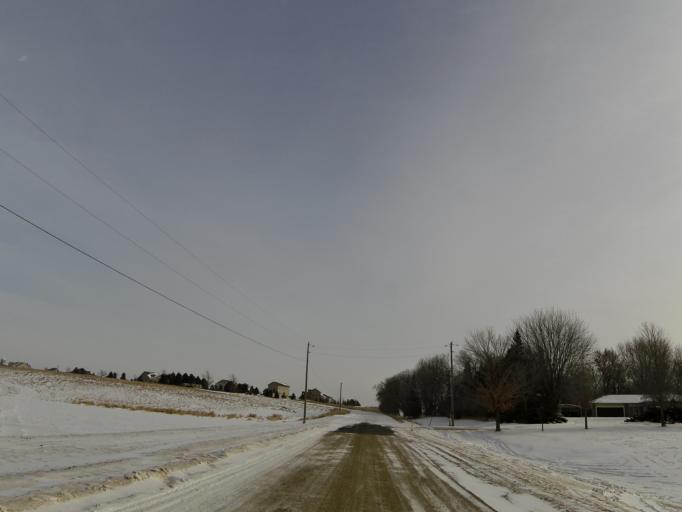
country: US
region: Minnesota
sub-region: Carver County
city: Mayer
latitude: 44.8912
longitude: -93.8817
